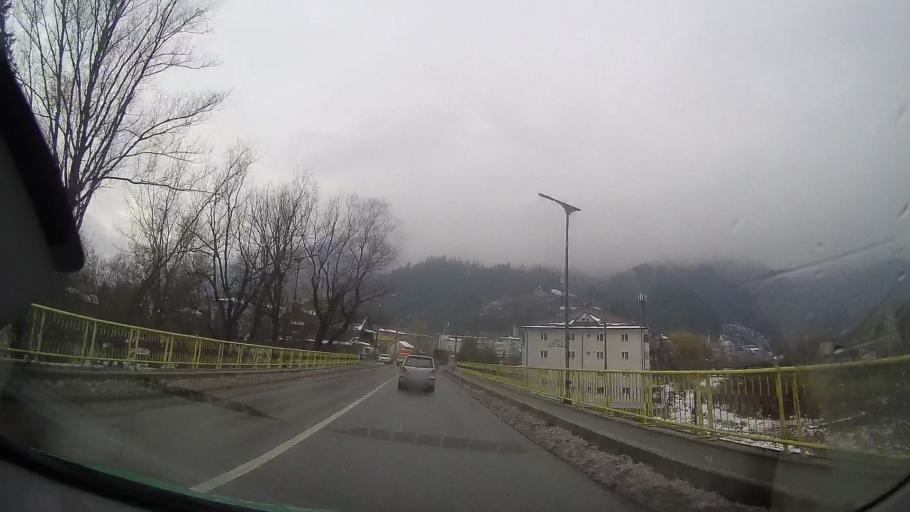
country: RO
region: Neamt
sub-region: Comuna Bicaz
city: Dodeni
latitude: 46.9108
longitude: 26.0914
